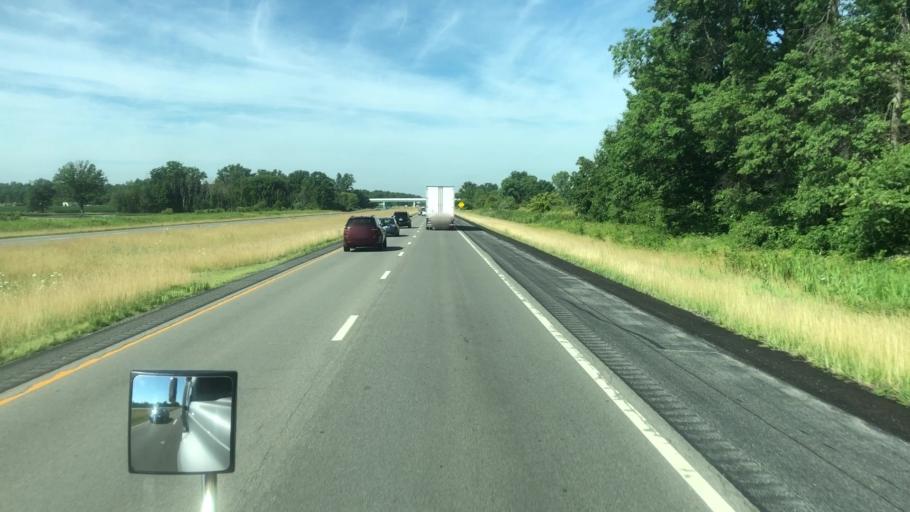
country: US
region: Ohio
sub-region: Lorain County
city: Vermilion
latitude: 41.3925
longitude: -82.4007
